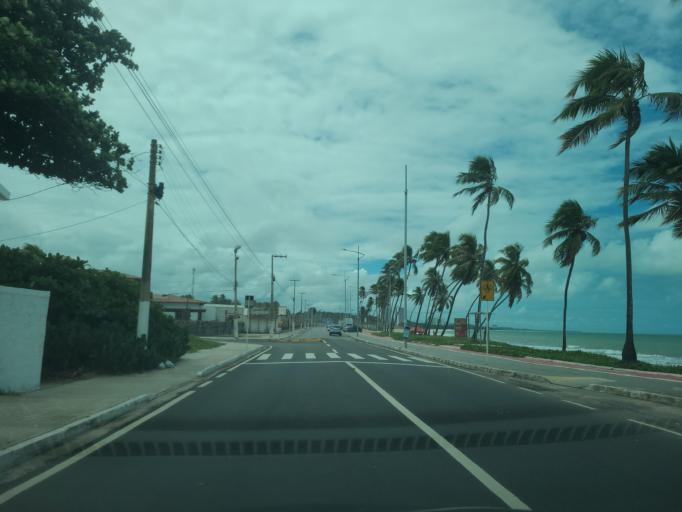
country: BR
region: Alagoas
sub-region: Maceio
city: Maceio
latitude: -9.6266
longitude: -35.6946
